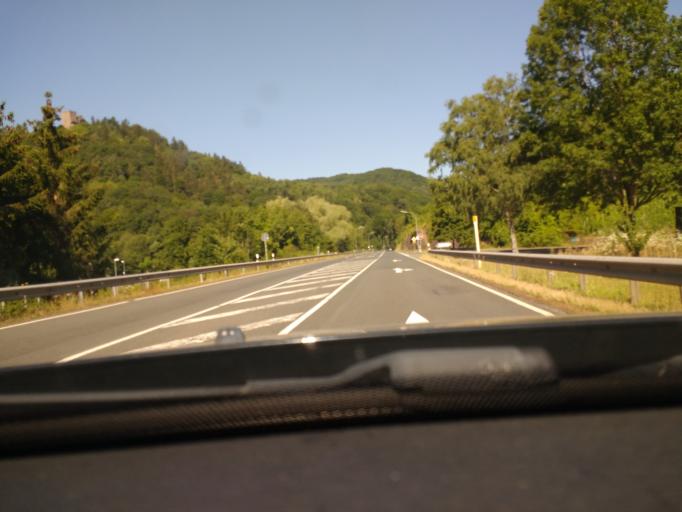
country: DE
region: Rheinland-Pfalz
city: Alf
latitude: 50.0529
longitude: 7.1143
